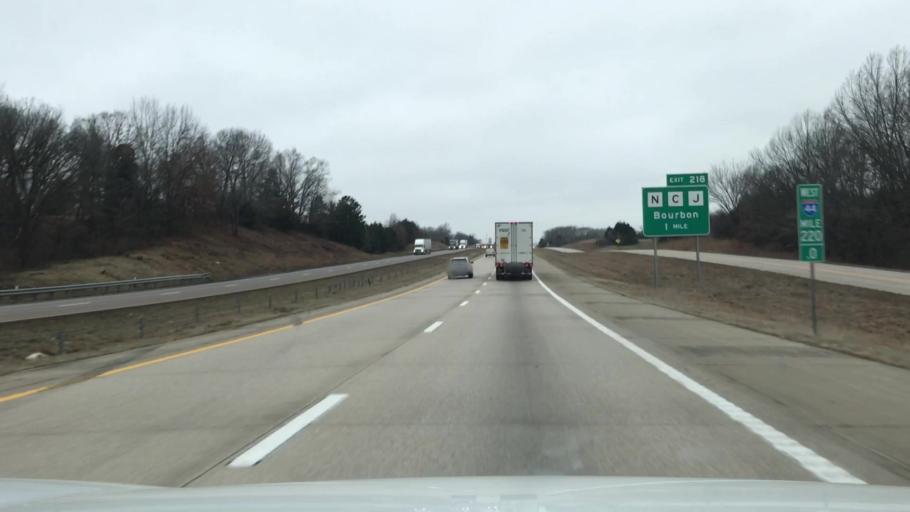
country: US
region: Missouri
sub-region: Crawford County
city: Bourbon
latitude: 38.1625
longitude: -91.2305
